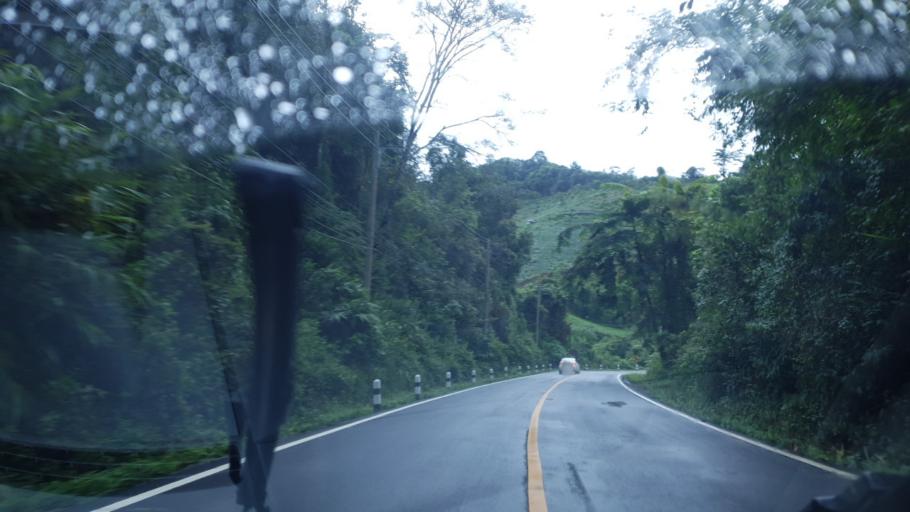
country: TH
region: Mae Hong Son
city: Ban Huai I Huak
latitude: 18.1439
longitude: 98.1145
